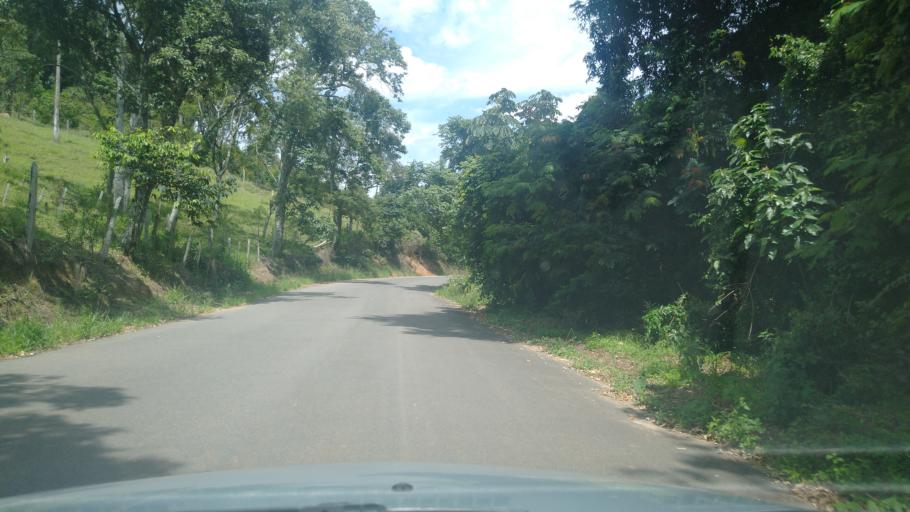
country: BR
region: Minas Gerais
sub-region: Extrema
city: Extrema
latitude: -22.7214
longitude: -46.3298
